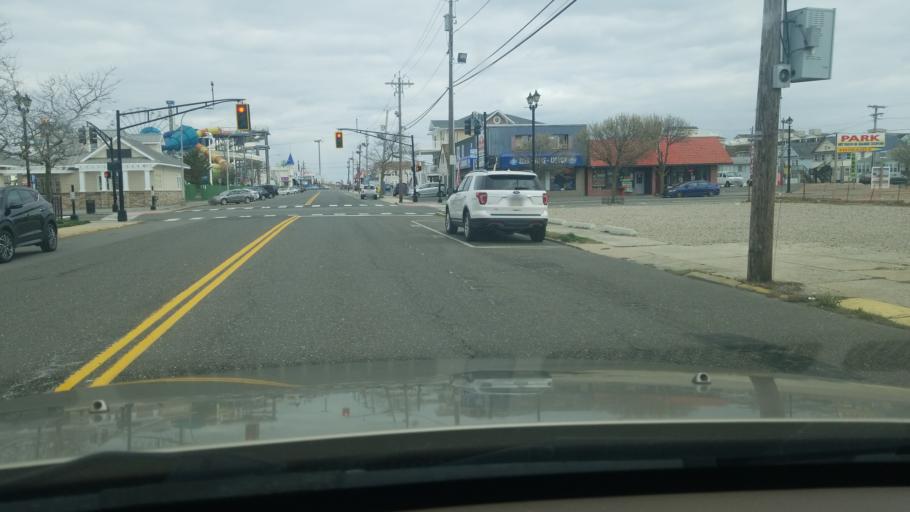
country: US
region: New Jersey
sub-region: Ocean County
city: Seaside Heights
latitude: 39.9427
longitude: -74.0740
